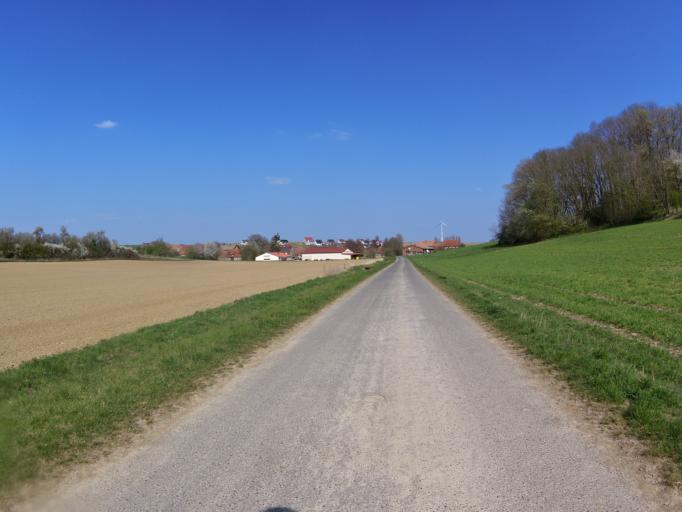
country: DE
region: Bavaria
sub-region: Regierungsbezirk Unterfranken
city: Mainstockheim
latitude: 49.8203
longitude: 10.1204
